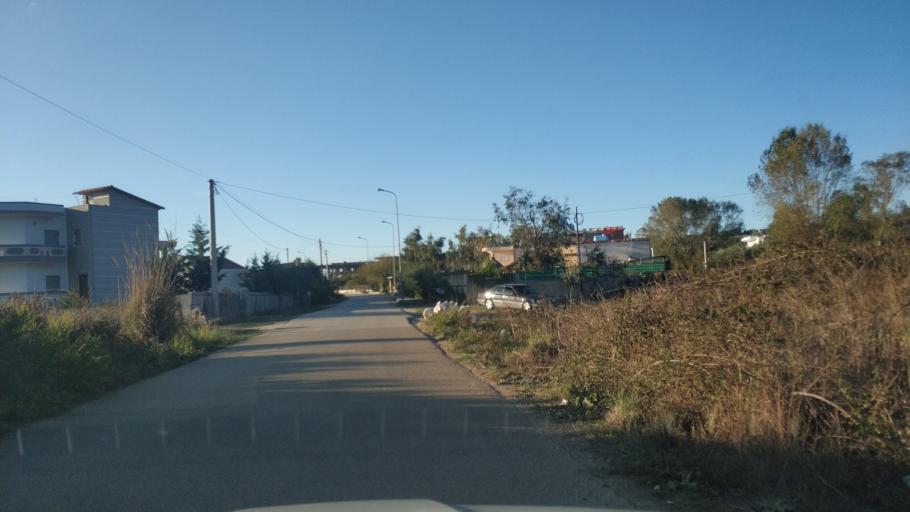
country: AL
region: Vlore
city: Vlore
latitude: 40.5054
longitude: 19.4146
